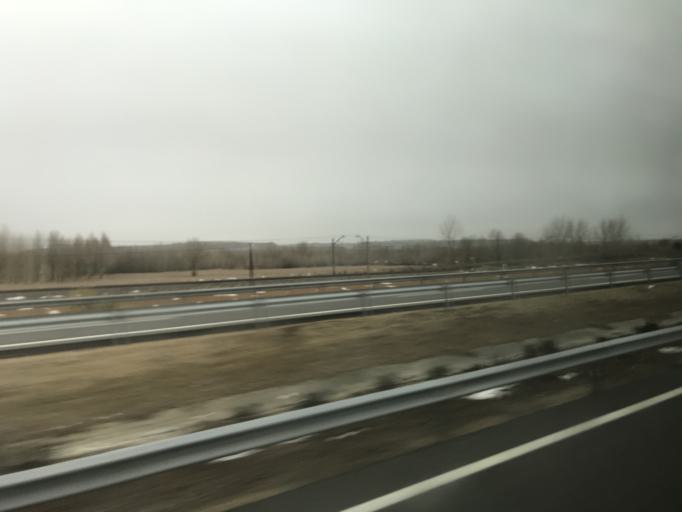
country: ES
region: Castille and Leon
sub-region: Provincia de Burgos
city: Villaverde-Mogina
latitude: 42.1821
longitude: -4.0465
